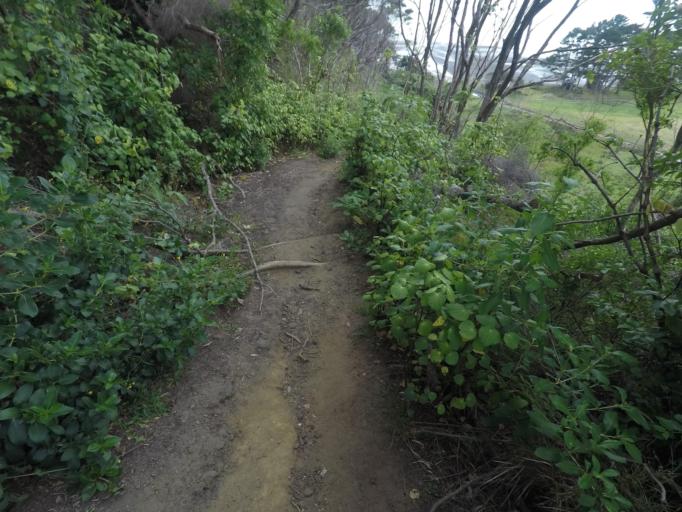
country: NZ
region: Auckland
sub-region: Auckland
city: Parakai
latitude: -36.4527
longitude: 174.2494
